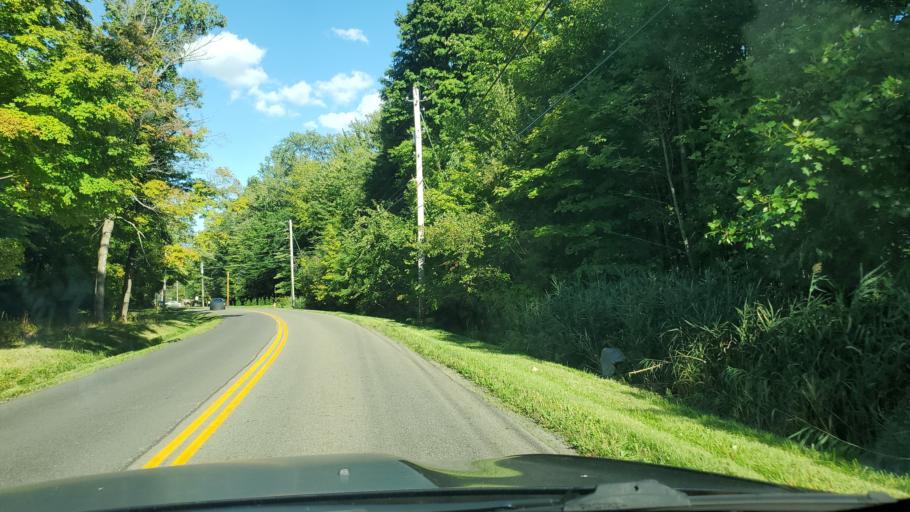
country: US
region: Ohio
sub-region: Mahoning County
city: Canfield
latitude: 41.0425
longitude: -80.7253
